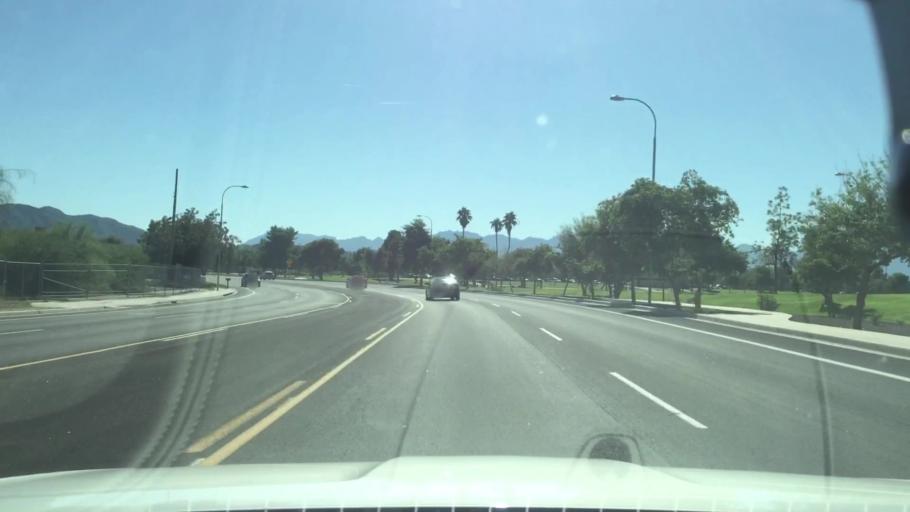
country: US
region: Arizona
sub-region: Maricopa County
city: Laveen
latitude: 33.3754
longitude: -112.1344
